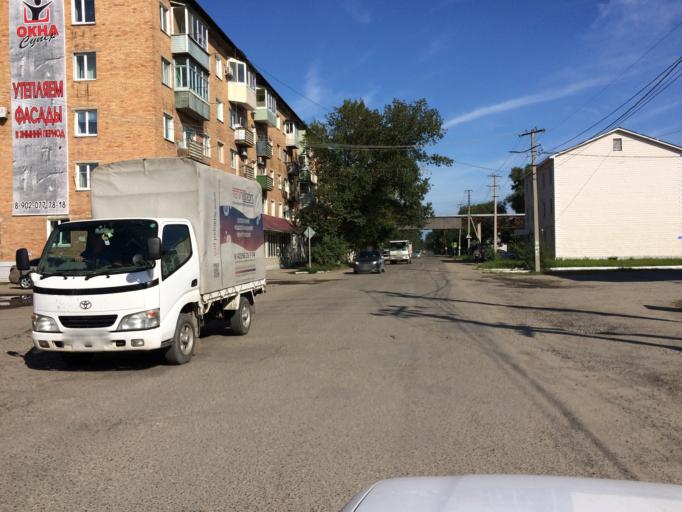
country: RU
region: Primorskiy
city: Dal'nerechensk
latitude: 45.9315
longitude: 133.7365
